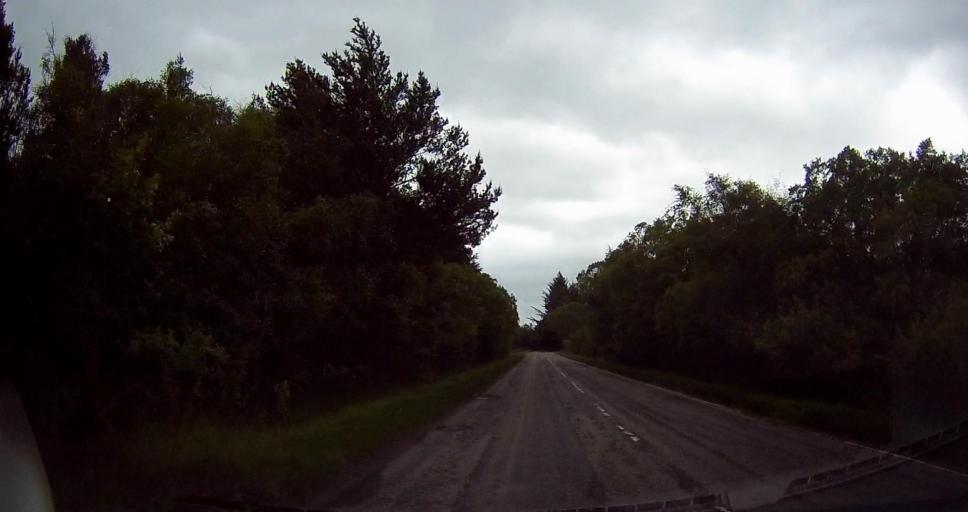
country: GB
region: Scotland
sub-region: Highland
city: Alness
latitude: 58.0419
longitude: -4.4244
